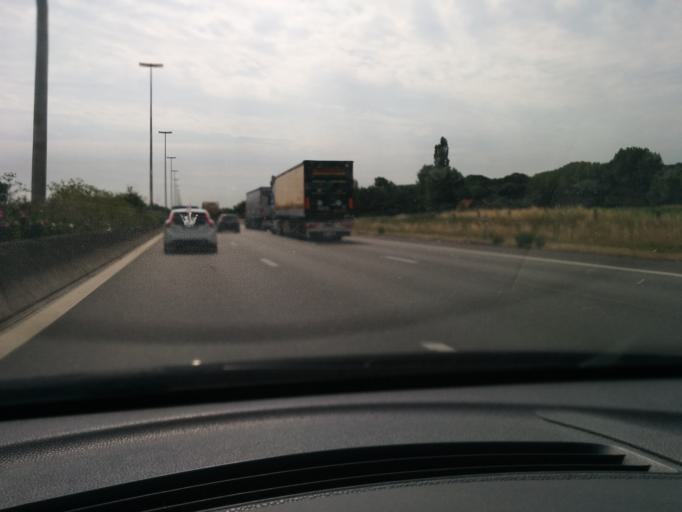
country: BE
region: Flanders
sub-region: Provincie West-Vlaanderen
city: Oostkamp
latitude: 51.1326
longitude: 3.2830
